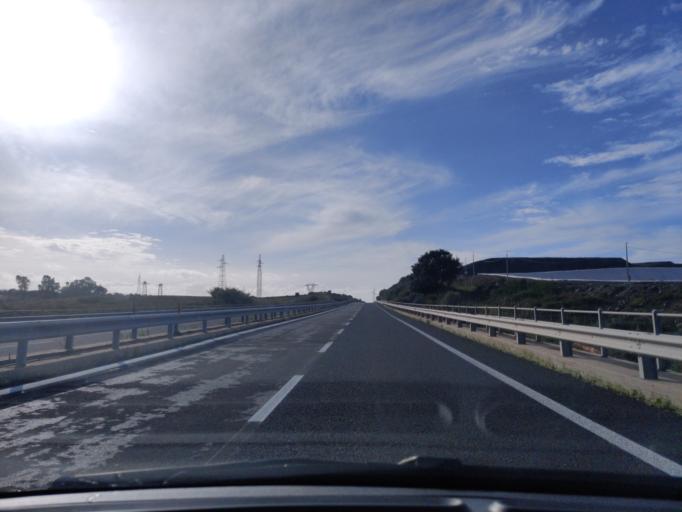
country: IT
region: Latium
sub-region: Citta metropolitana di Roma Capitale
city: Aurelia
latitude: 42.1181
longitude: 11.7915
